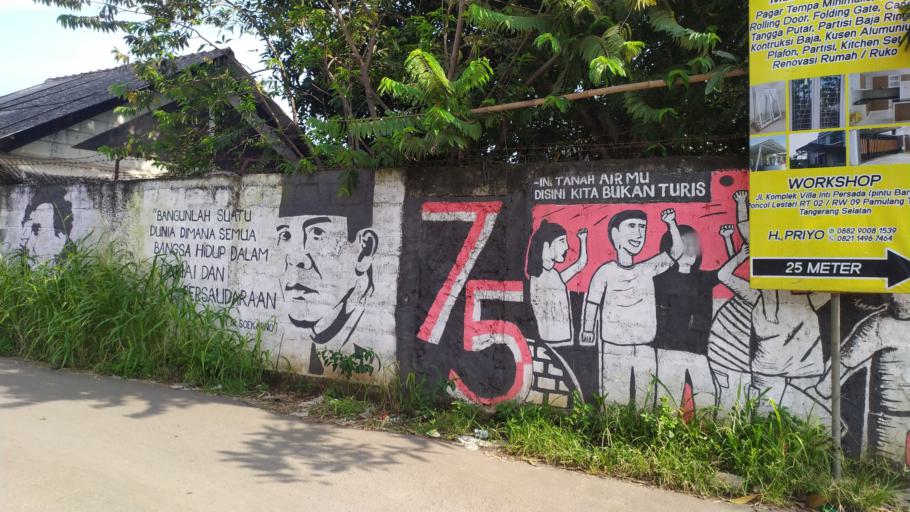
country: ID
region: West Java
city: Pamulang
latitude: -6.3590
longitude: 106.7426
